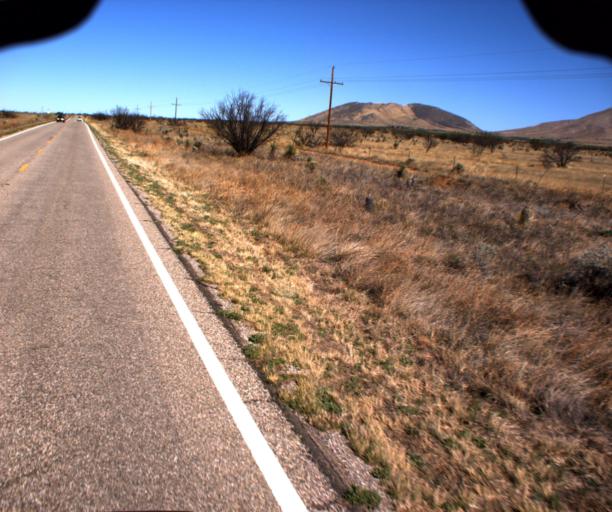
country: US
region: Arizona
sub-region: Cochise County
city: Huachuca City
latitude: 31.7039
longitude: -110.4360
